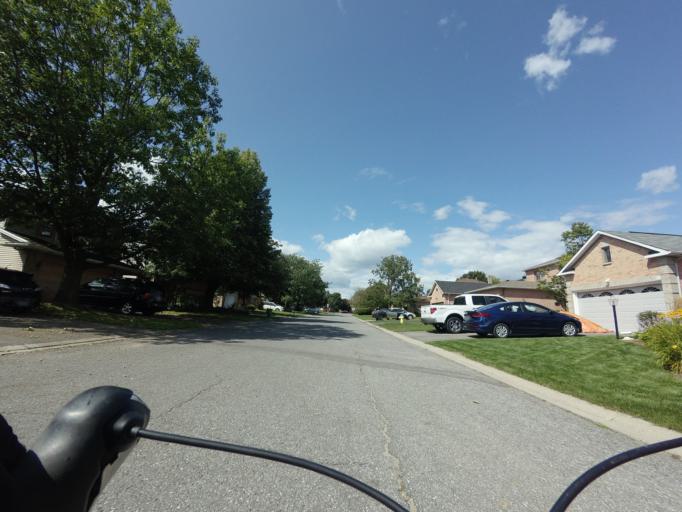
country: CA
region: Ontario
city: Bells Corners
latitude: 45.2896
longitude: -75.8679
